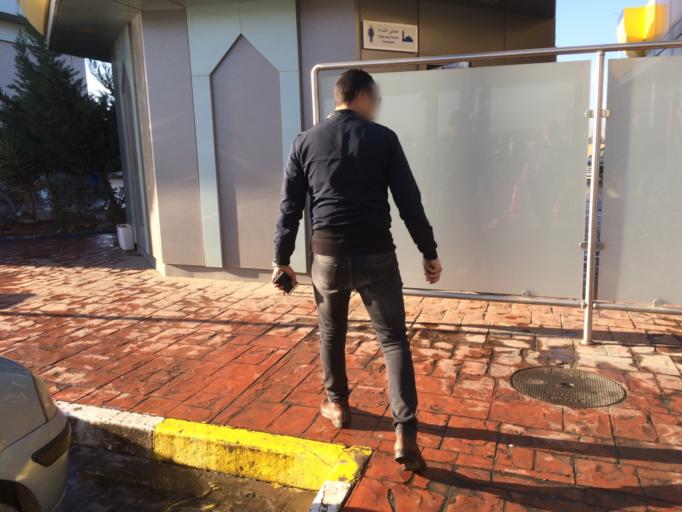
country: DZ
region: Chlef
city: Oued Sly
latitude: 36.0929
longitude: 1.2001
